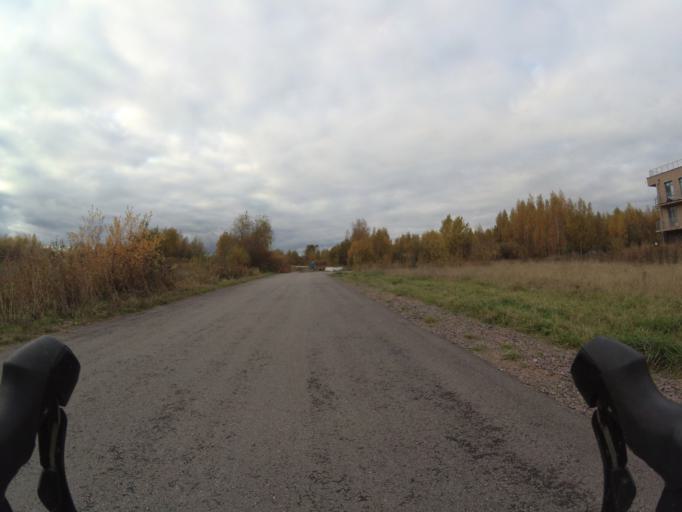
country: RU
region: St.-Petersburg
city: Lakhtinskiy
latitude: 60.0049
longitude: 30.1507
